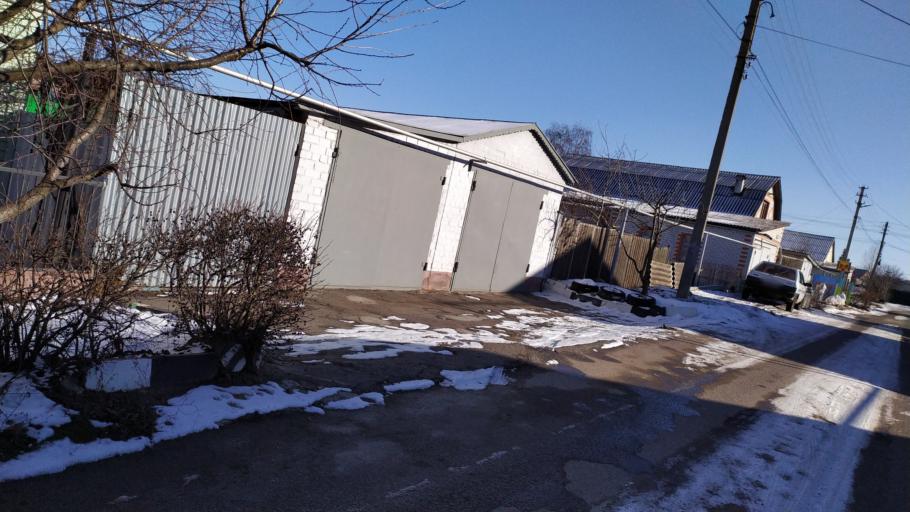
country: RU
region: Kursk
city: Kursk
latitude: 51.6408
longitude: 36.1447
